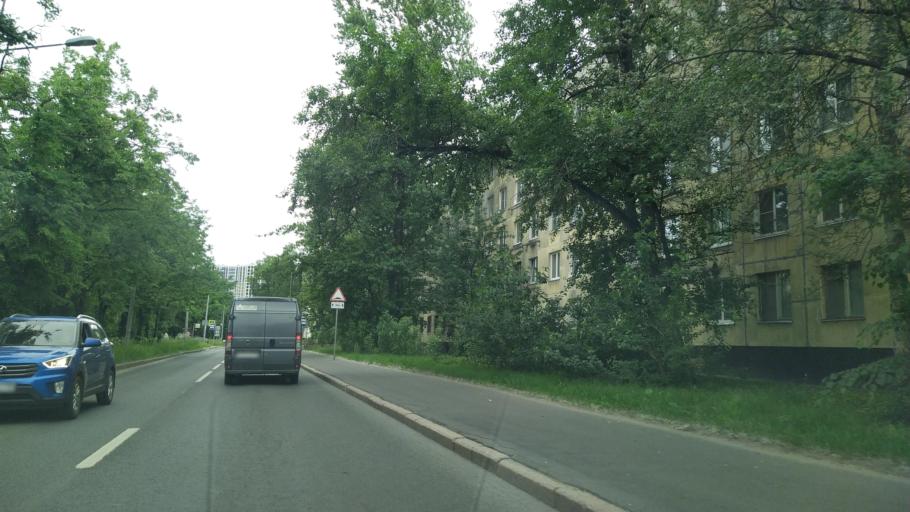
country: RU
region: St.-Petersburg
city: Avtovo
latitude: 59.8455
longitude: 30.3031
